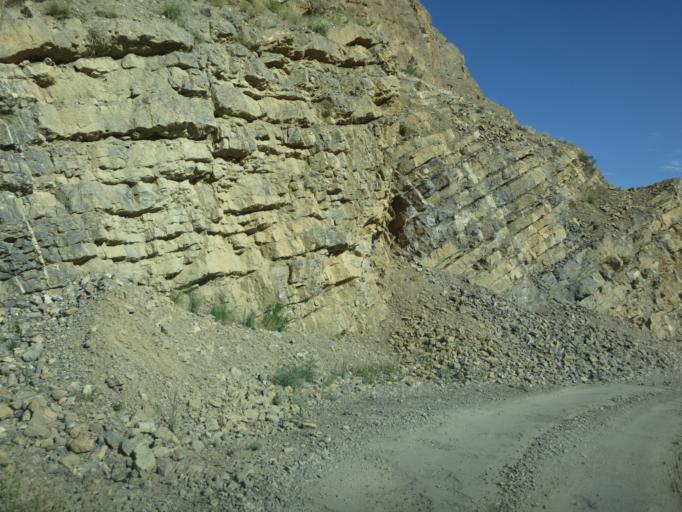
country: IN
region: Himachal Pradesh
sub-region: Kulu
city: Manali
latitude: 32.3160
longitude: 78.0027
